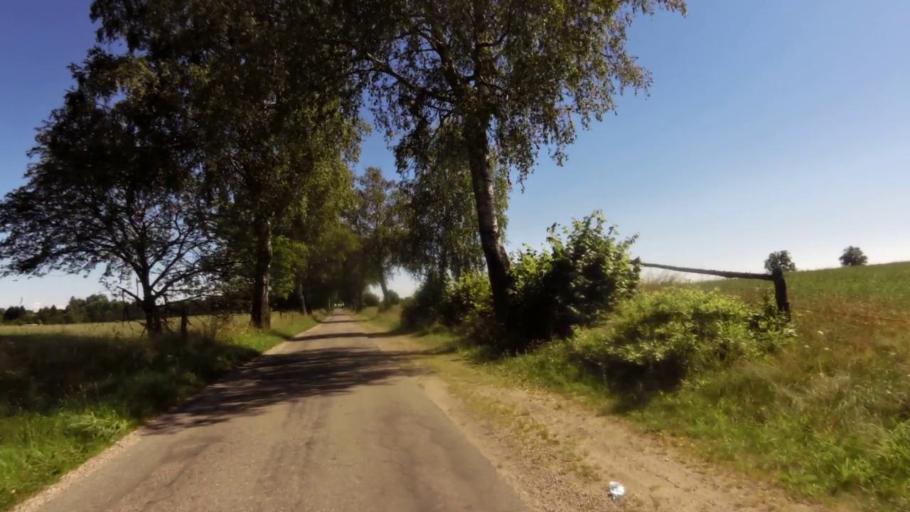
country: PL
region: West Pomeranian Voivodeship
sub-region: Powiat szczecinecki
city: Bialy Bor
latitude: 53.8879
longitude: 16.9245
